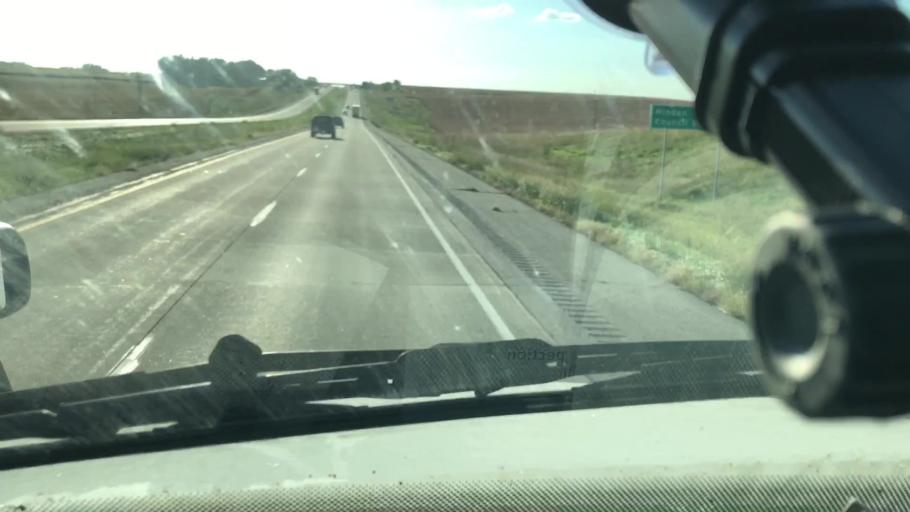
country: US
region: Iowa
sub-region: Pottawattamie County
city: Avoca
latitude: 41.4991
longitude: -95.4671
